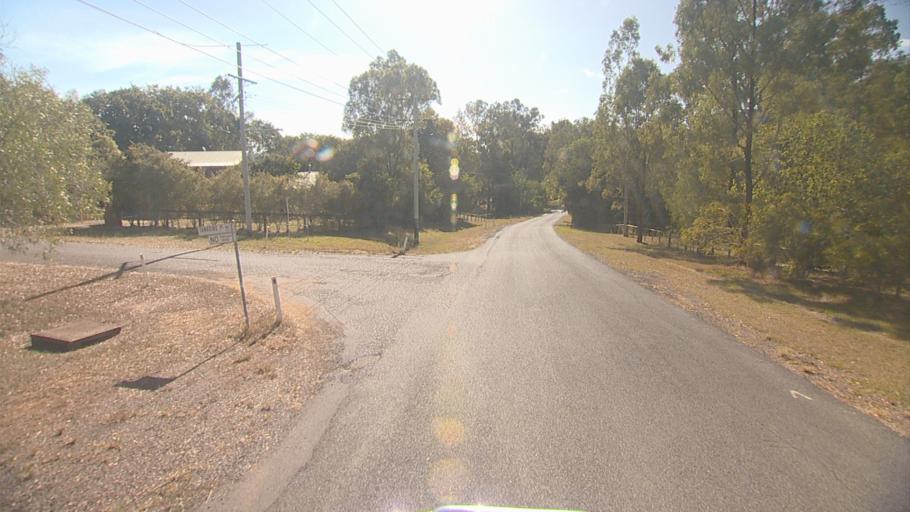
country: AU
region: Queensland
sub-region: Logan
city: Cedar Vale
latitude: -27.8533
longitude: 152.9861
